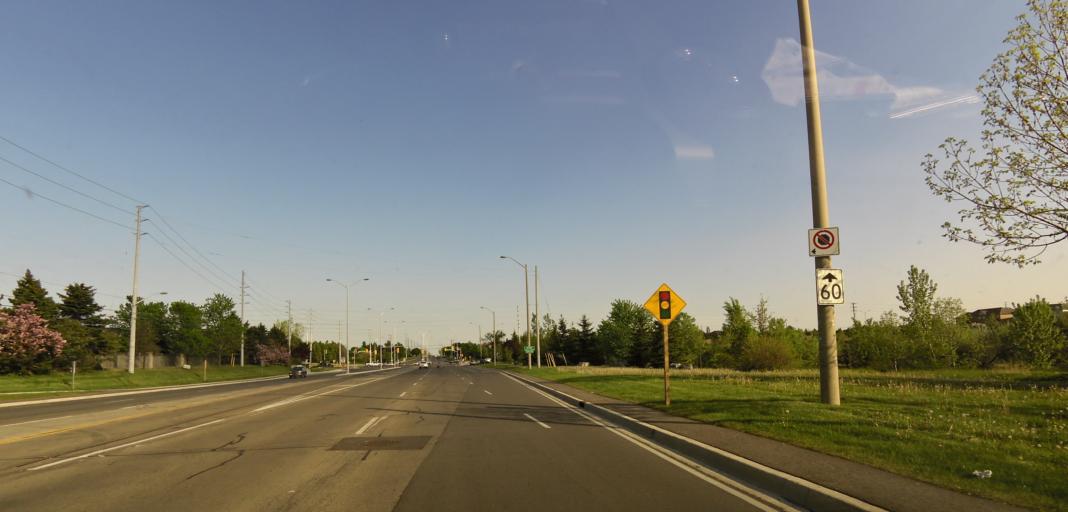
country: CA
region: Ontario
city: Brampton
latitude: 43.7360
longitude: -79.7567
